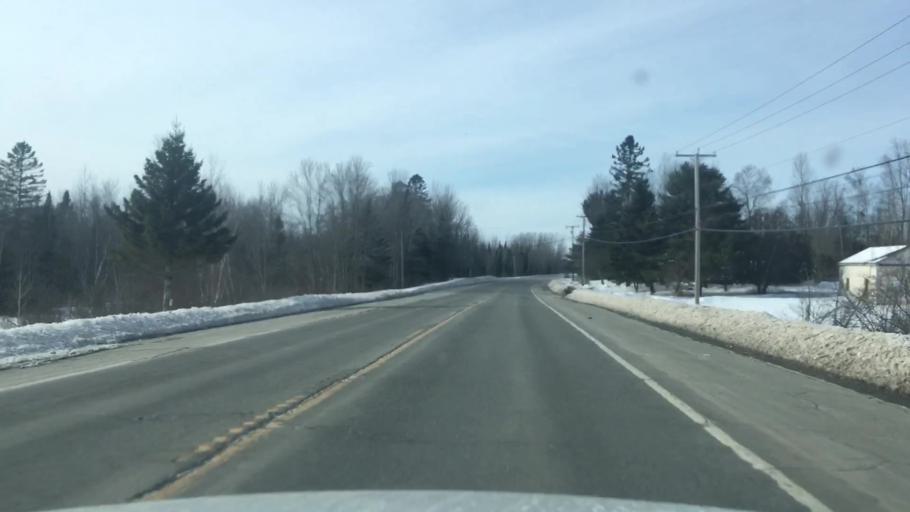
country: US
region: Maine
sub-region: Penobscot County
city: Kenduskeag
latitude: 44.9062
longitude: -68.8923
